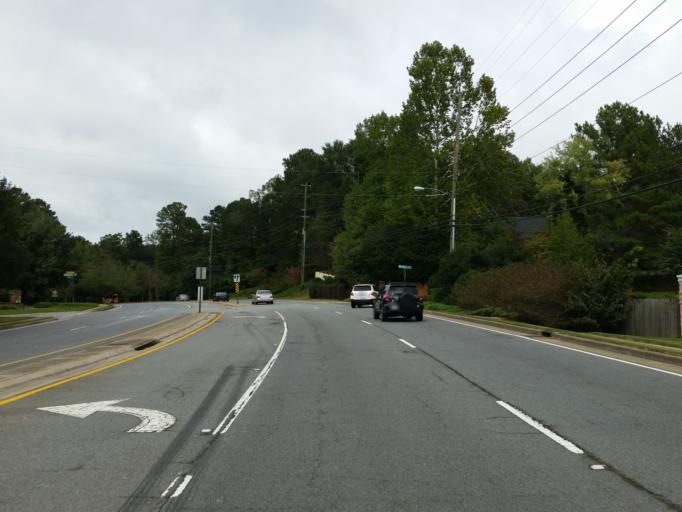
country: US
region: Georgia
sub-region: Fulton County
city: Roswell
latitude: 33.9988
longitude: -84.4343
